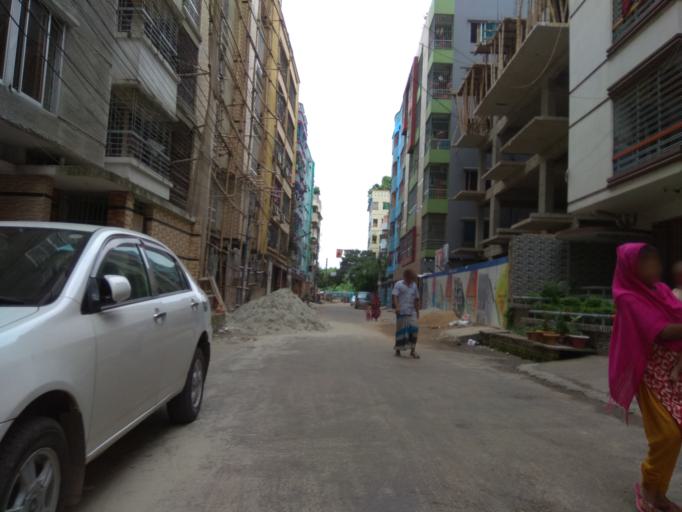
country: BD
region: Dhaka
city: Azimpur
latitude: 23.8121
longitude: 90.3564
